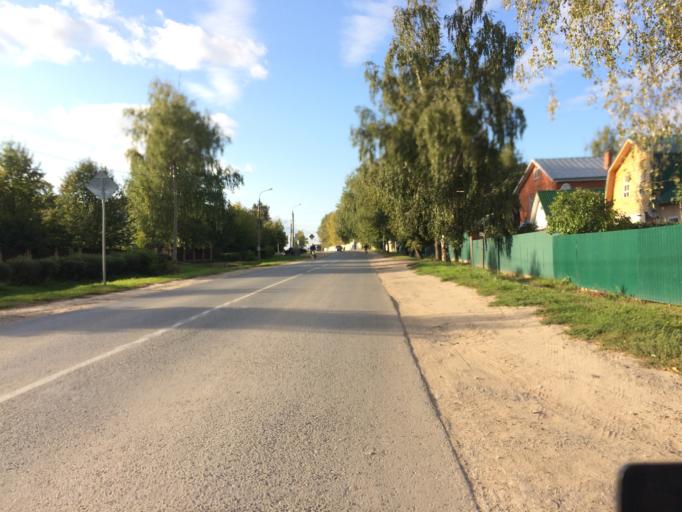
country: RU
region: Mariy-El
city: Yoshkar-Ola
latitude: 56.6520
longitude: 47.9792
